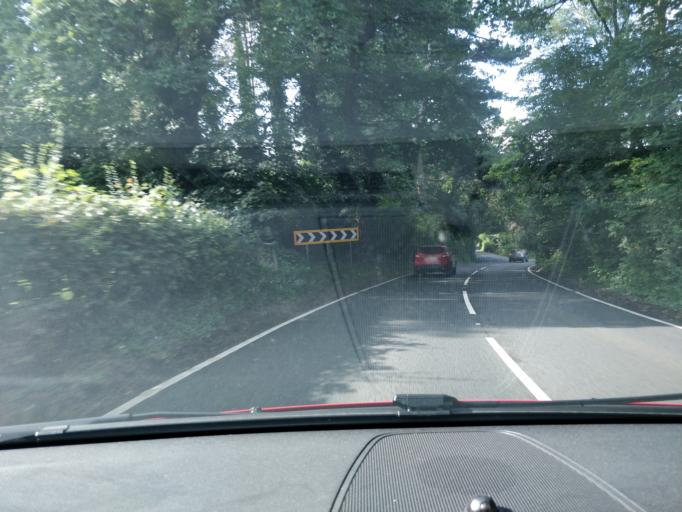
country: GB
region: Wales
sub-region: Conwy
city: Llansantffraid Glan Conwy
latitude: 53.2424
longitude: -3.7965
